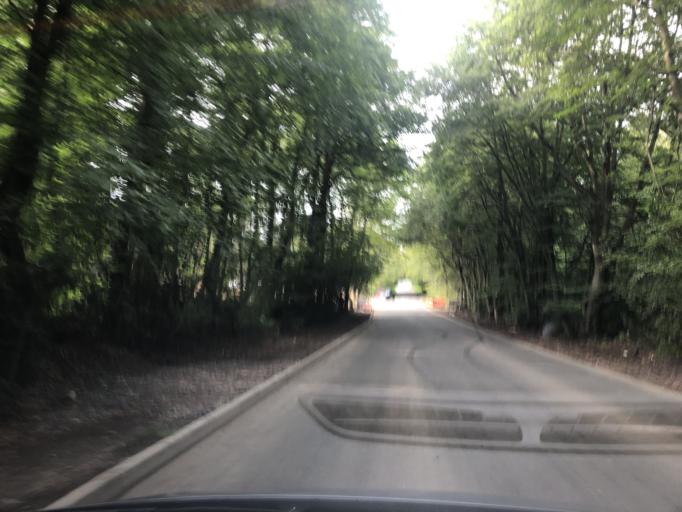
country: GB
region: Scotland
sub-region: Midlothian
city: Penicuik
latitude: 55.8454
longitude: -3.2261
